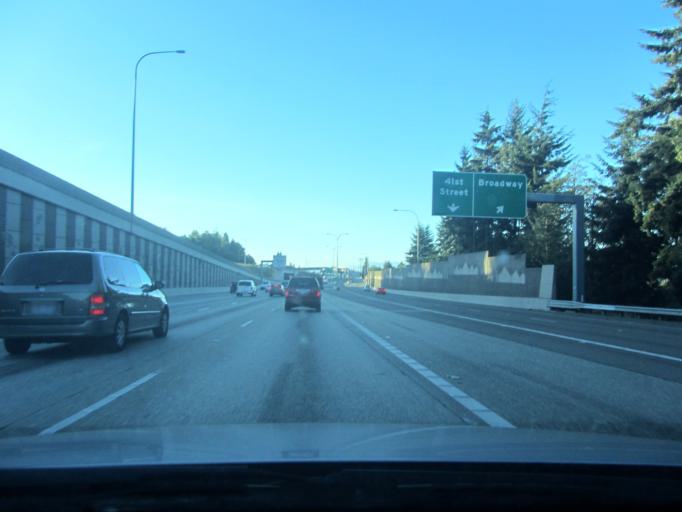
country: US
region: Washington
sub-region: Snohomish County
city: Everett
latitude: 47.9550
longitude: -122.1993
